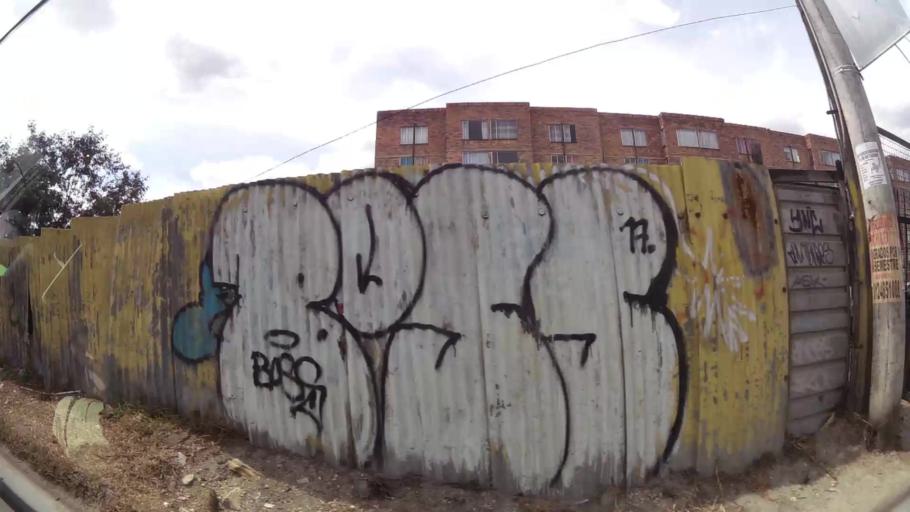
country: CO
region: Cundinamarca
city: Soacha
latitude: 4.6413
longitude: -74.1650
